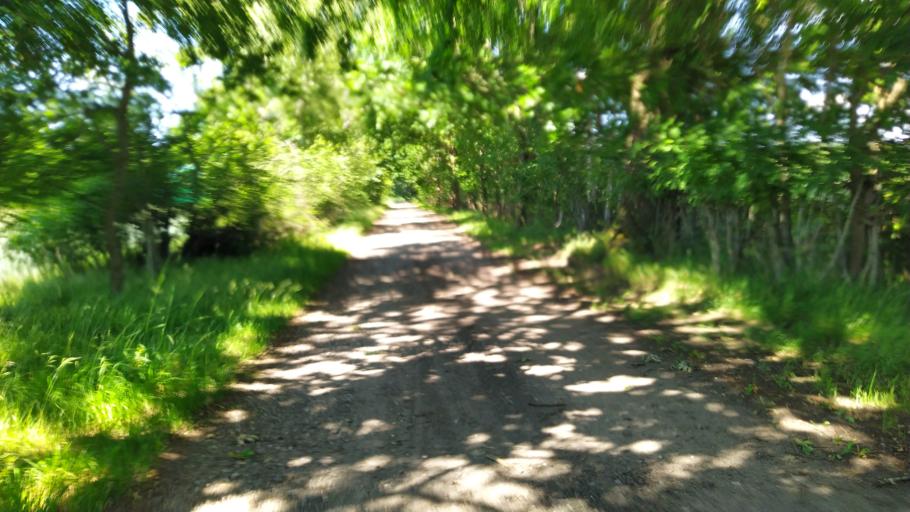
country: DE
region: Lower Saxony
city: Oldendorf
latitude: 53.5666
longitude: 9.2478
